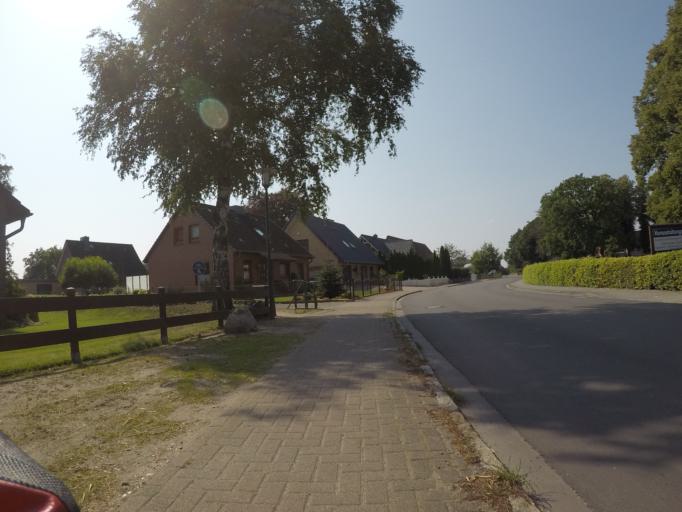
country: DE
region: Schleswig-Holstein
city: Stuvenborn
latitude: 53.8513
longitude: 10.1233
